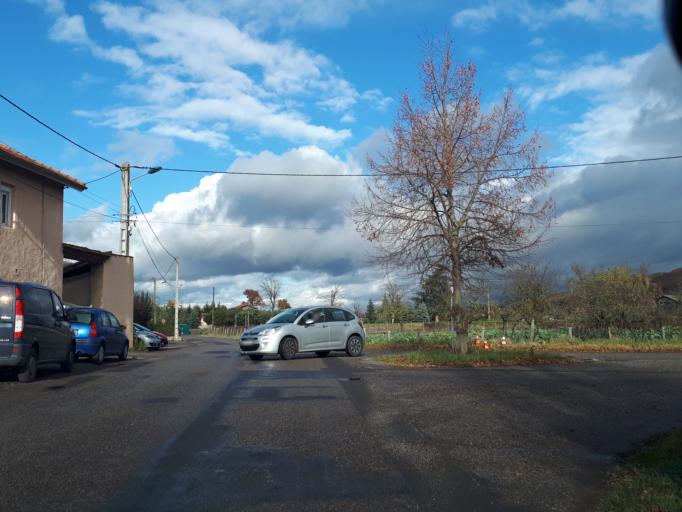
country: FR
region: Rhone-Alpes
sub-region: Departement de la Loire
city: Bellegarde-en-Forez
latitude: 45.6452
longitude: 4.2920
